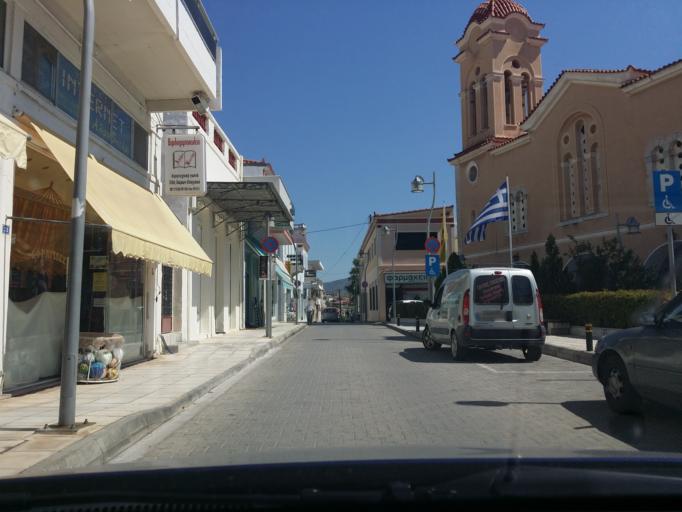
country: GR
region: Peloponnese
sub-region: Nomos Lakonias
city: Molaoi
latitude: 36.8041
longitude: 22.8517
